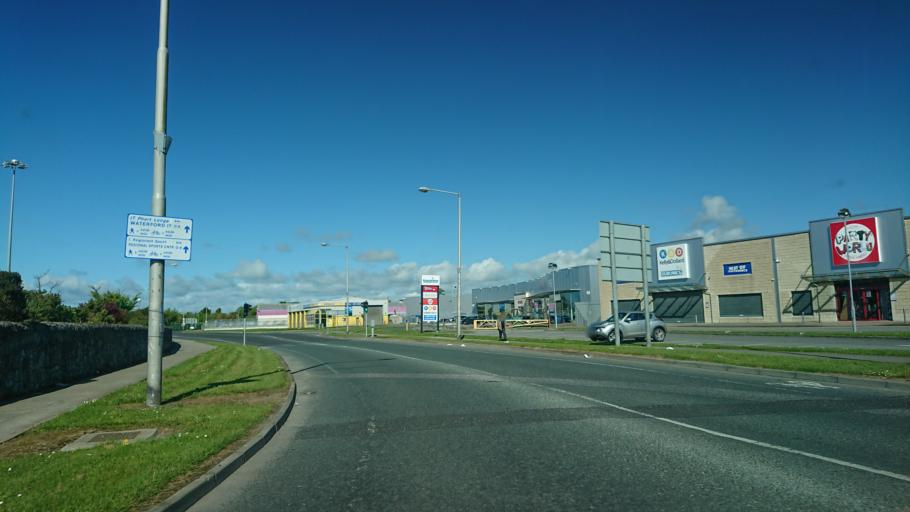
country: IE
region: Munster
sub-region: Waterford
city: Waterford
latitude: 52.2472
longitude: -7.1202
